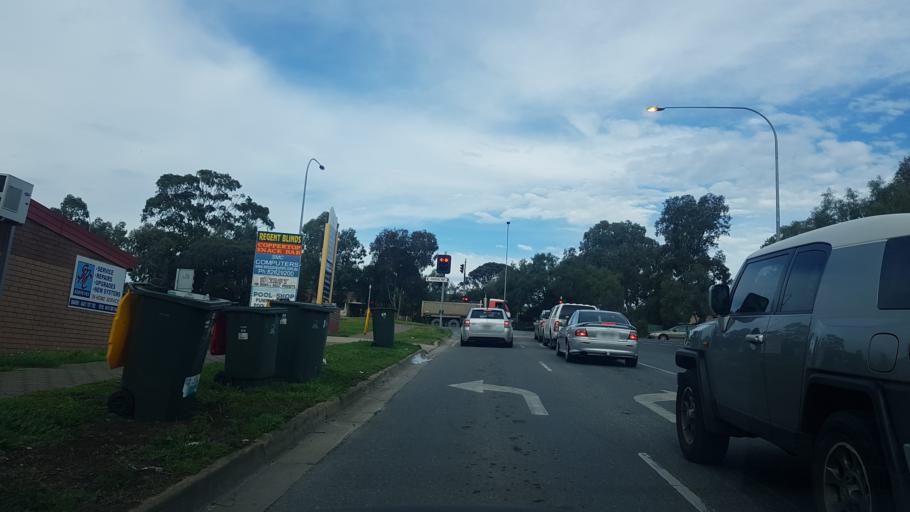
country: AU
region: South Australia
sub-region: Salisbury
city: Ingle Farm
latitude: -34.8190
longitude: 138.6396
